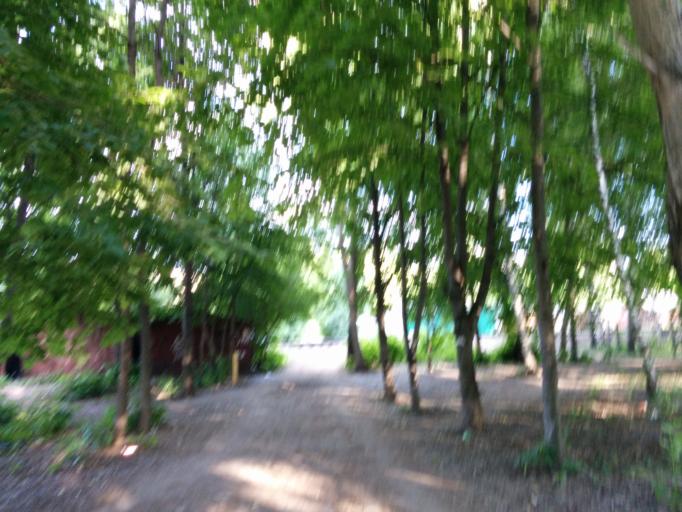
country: RU
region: Tambov
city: Tambov
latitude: 52.7470
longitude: 41.4417
